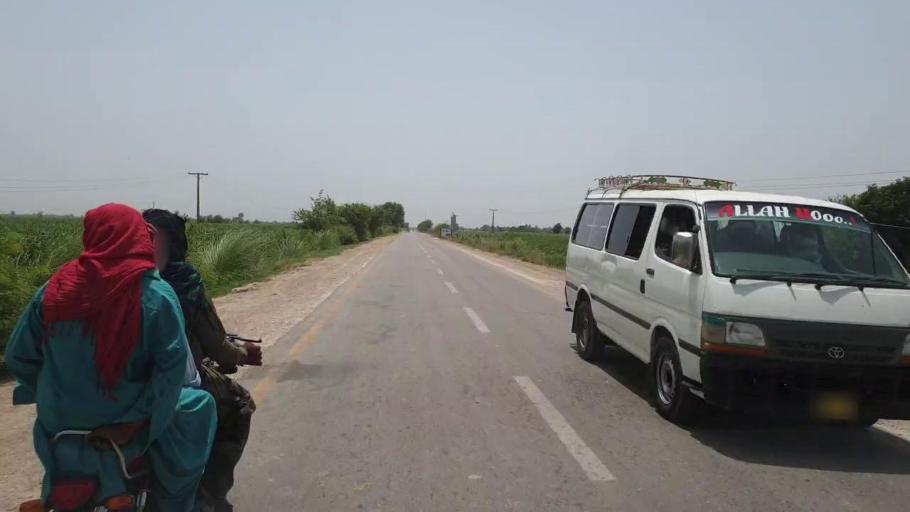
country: PK
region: Sindh
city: Moro
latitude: 26.6000
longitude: 68.0881
